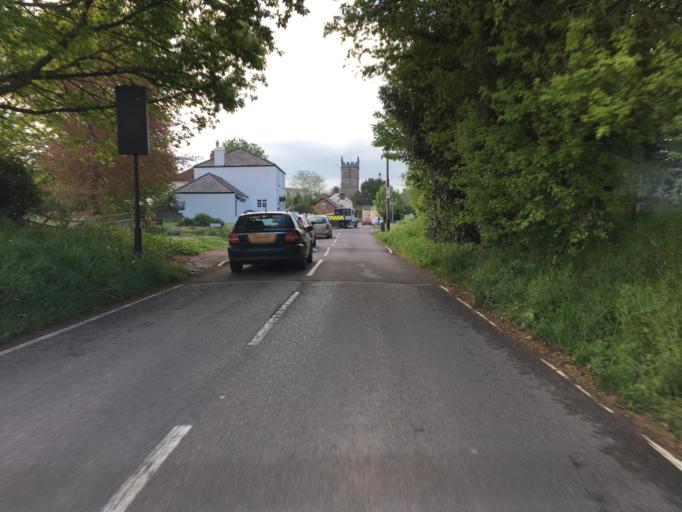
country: GB
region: Wales
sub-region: Monmouthshire
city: Llanarth
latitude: 51.7629
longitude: -2.8503
